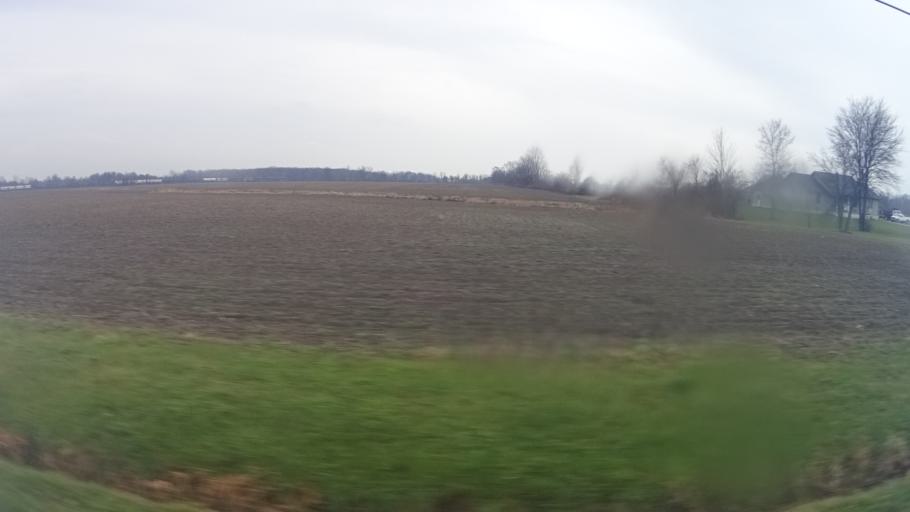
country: US
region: Ohio
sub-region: Lorain County
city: Lagrange
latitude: 41.2223
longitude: -82.1516
